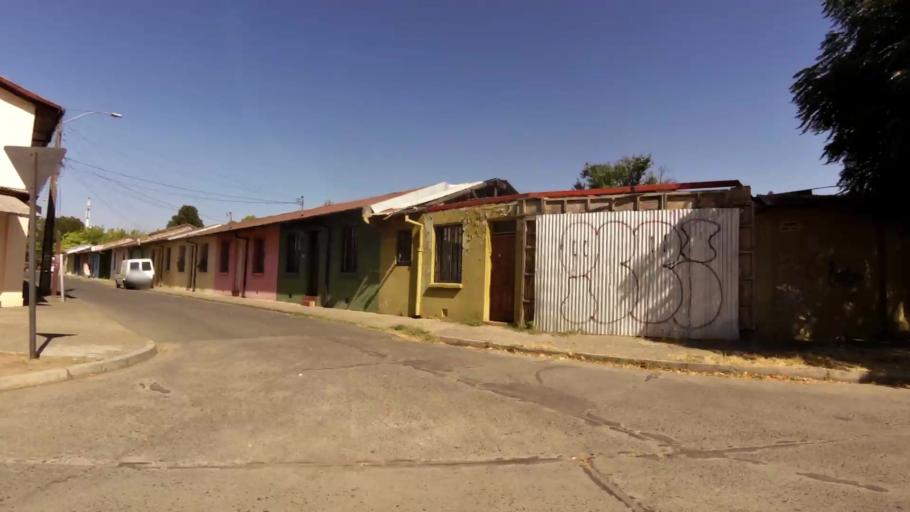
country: CL
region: Maule
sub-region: Provincia de Talca
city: Talca
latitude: -35.4170
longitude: -71.6642
